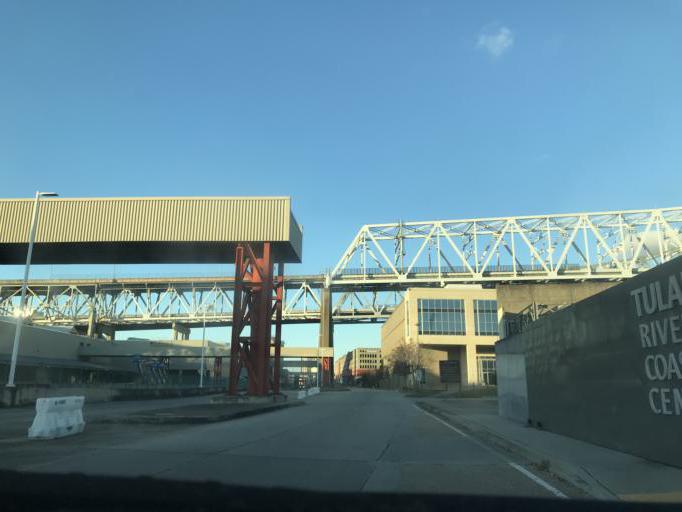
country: US
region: Louisiana
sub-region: Jefferson Parish
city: Gretna
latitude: 29.9357
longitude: -90.0618
